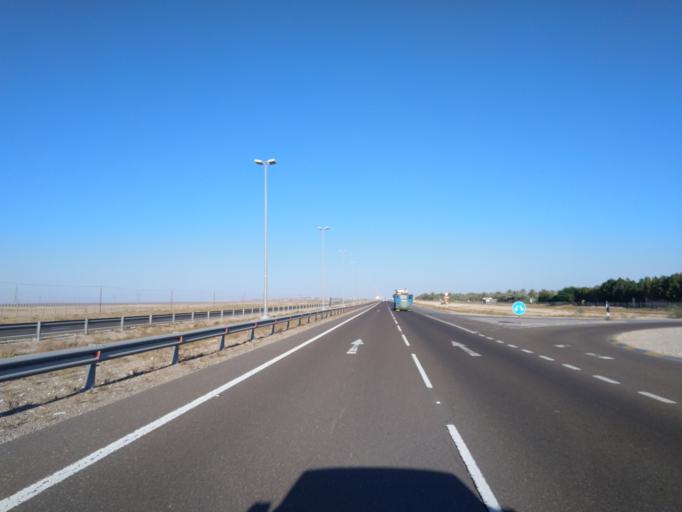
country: OM
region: Al Buraimi
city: Al Buraymi
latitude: 24.4904
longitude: 55.4070
